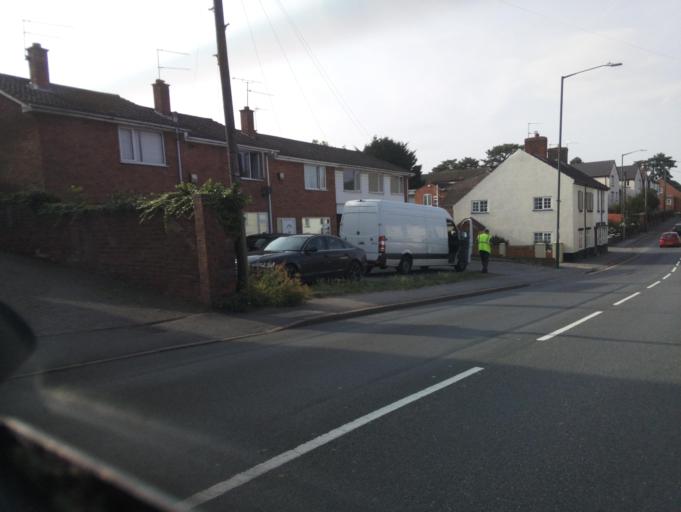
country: GB
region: England
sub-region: Warwickshire
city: Studley
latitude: 52.2703
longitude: -1.8936
